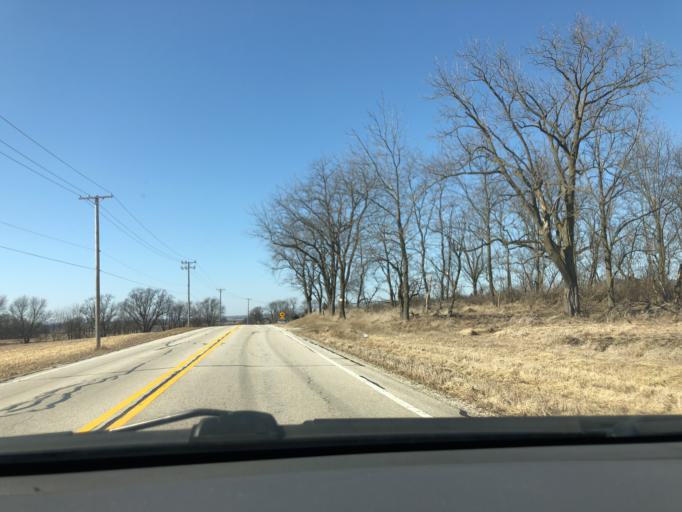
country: US
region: Illinois
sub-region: Kane County
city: Hampshire
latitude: 42.1246
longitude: -88.5068
